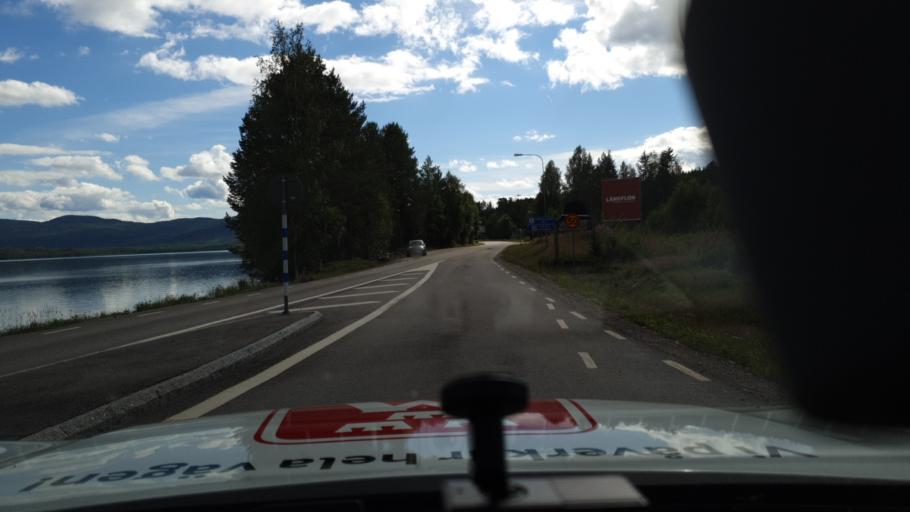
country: NO
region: Hedmark
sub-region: Trysil
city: Innbygda
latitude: 61.0454
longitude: 12.5951
